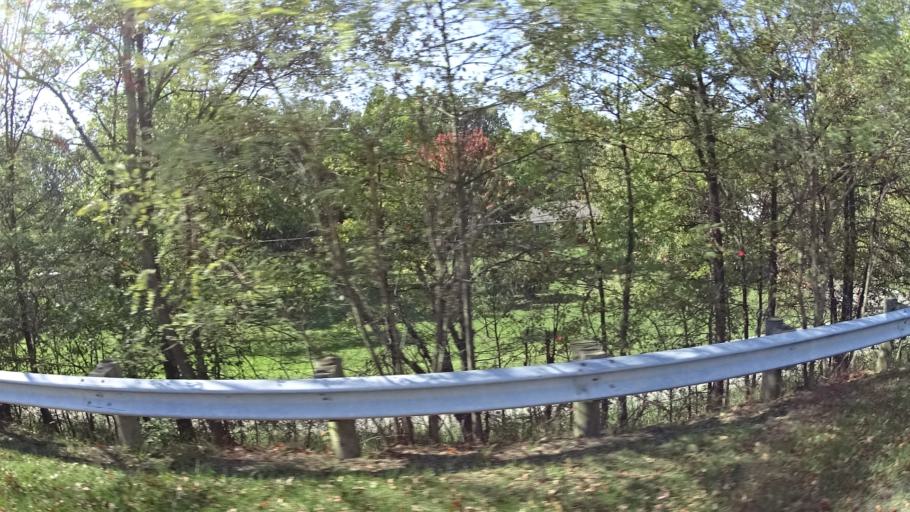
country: US
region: Ohio
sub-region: Lorain County
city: Vermilion-on-the-Lake
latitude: 41.4046
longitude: -82.2965
